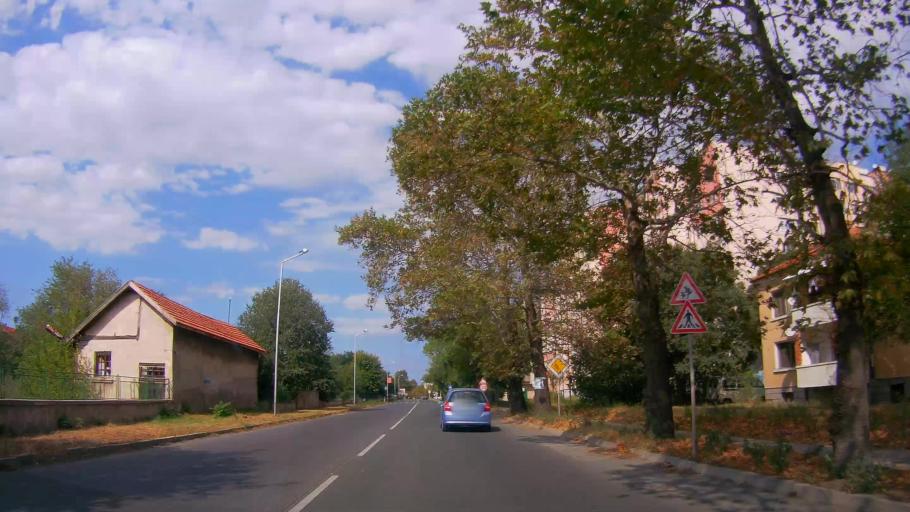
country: BG
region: Burgas
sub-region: Obshtina Aytos
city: Aytos
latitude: 42.6975
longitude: 27.2579
